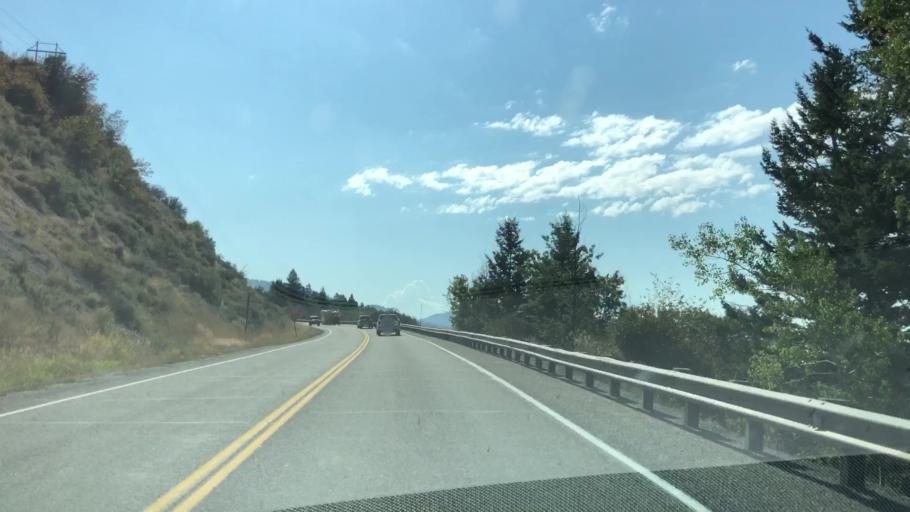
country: US
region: Idaho
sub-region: Teton County
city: Victor
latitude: 43.3127
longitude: -111.1455
